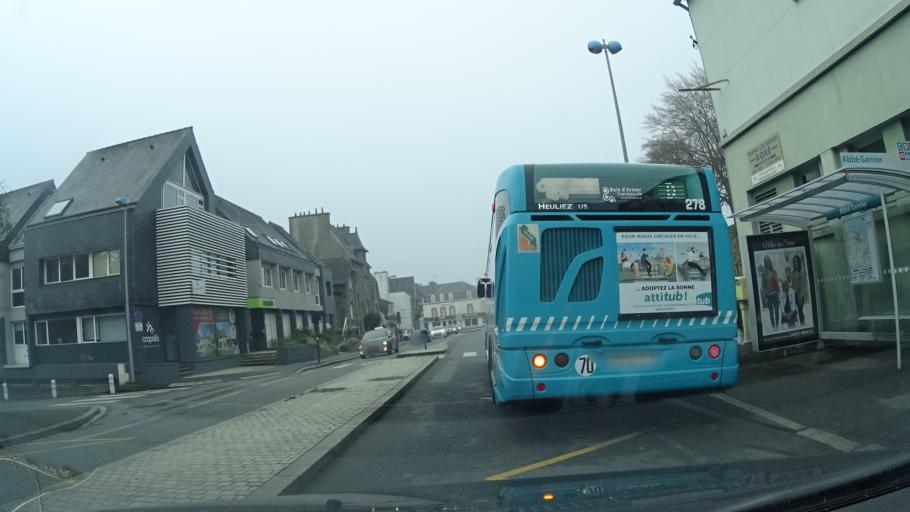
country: FR
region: Brittany
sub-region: Departement des Cotes-d'Armor
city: Saint-Brieuc
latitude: 48.5047
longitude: -2.7620
